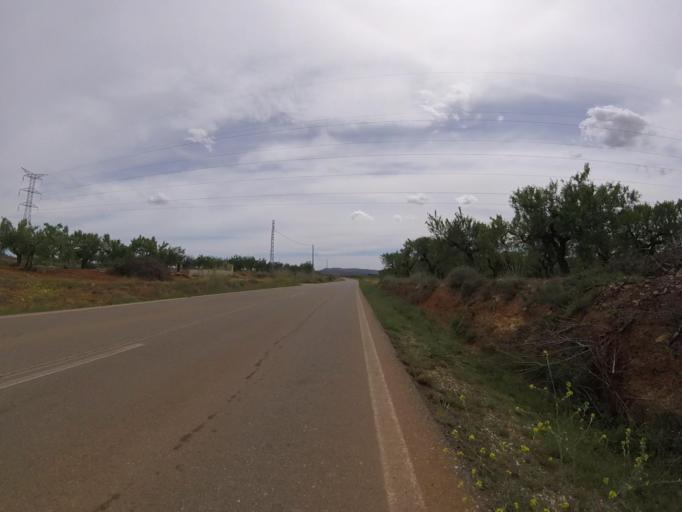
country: ES
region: Valencia
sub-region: Provincia de Castello
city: Cabanes
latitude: 40.1698
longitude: -0.0002
